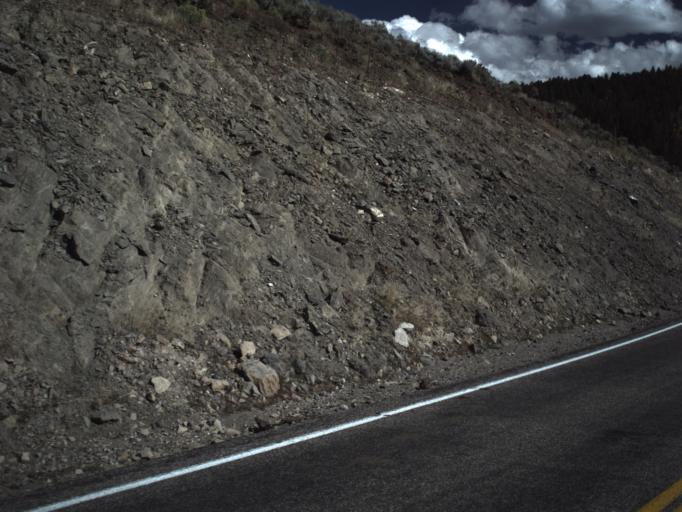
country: US
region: Utah
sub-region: Garfield County
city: Panguitch
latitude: 37.7194
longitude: -112.6257
